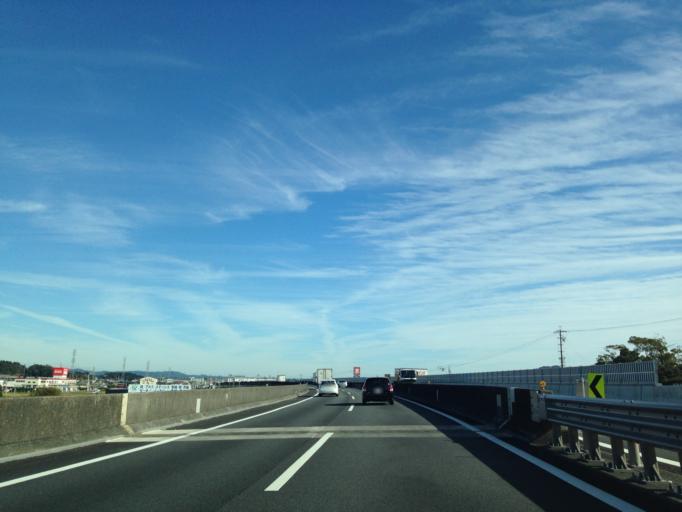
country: JP
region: Shizuoka
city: Fukuroi
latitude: 34.7571
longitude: 137.9330
